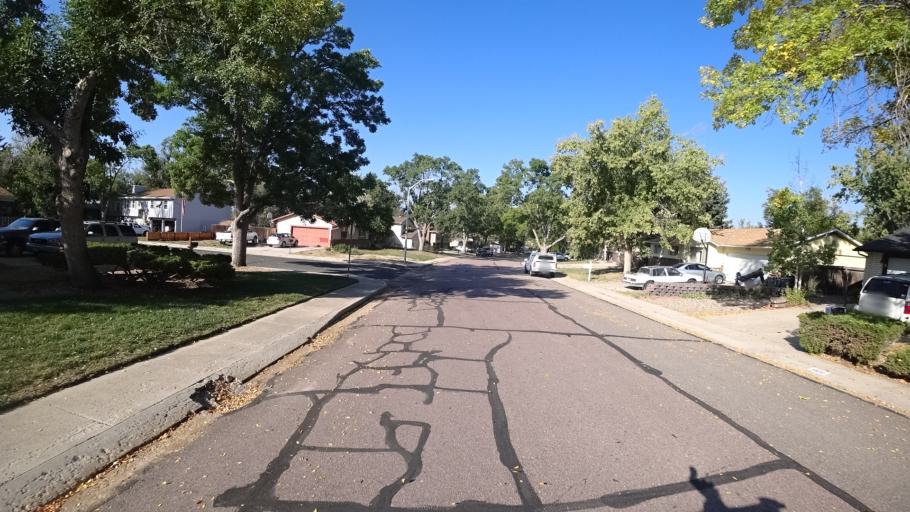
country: US
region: Colorado
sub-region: El Paso County
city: Cimarron Hills
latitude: 38.8778
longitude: -104.7411
